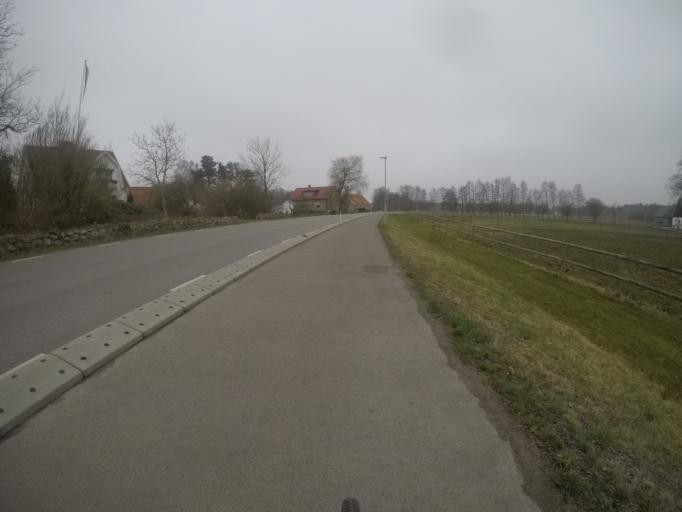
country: SE
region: Skane
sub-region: Angelholms Kommun
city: Vejbystrand
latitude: 56.2166
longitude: 12.7132
